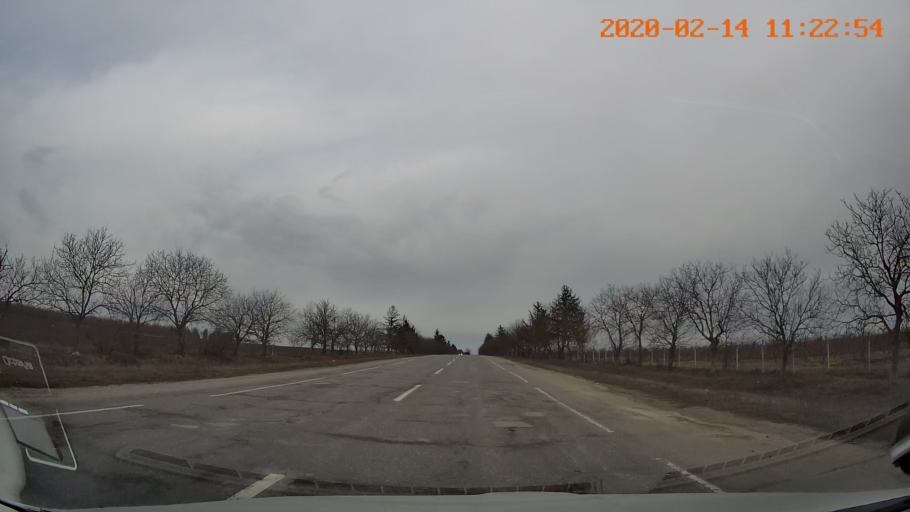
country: MD
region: Briceni
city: Briceni
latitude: 48.3161
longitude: 27.1217
